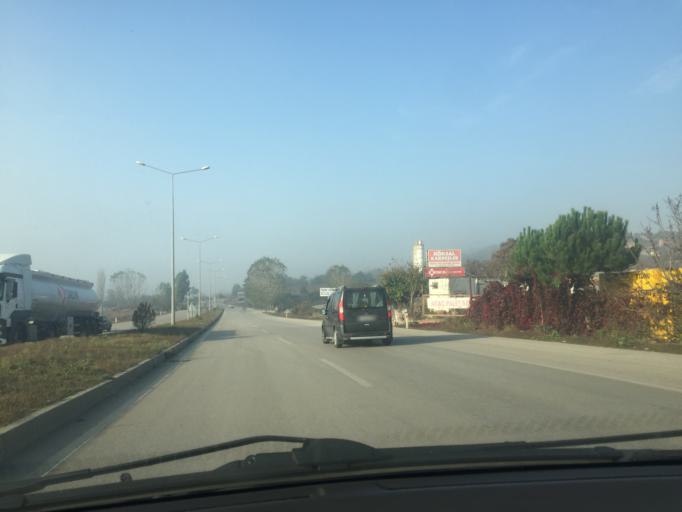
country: TR
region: Canakkale
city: Can
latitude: 40.0064
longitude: 27.0512
